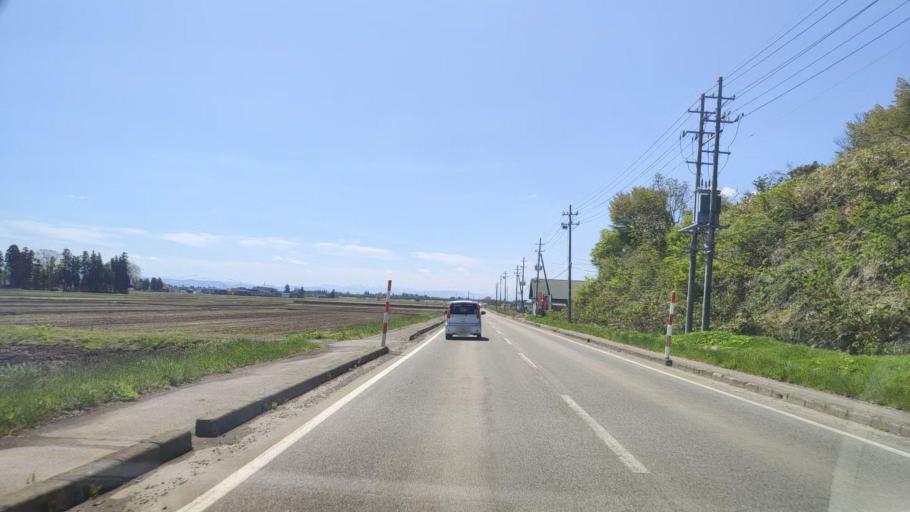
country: JP
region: Akita
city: Omagari
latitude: 39.4446
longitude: 140.4481
